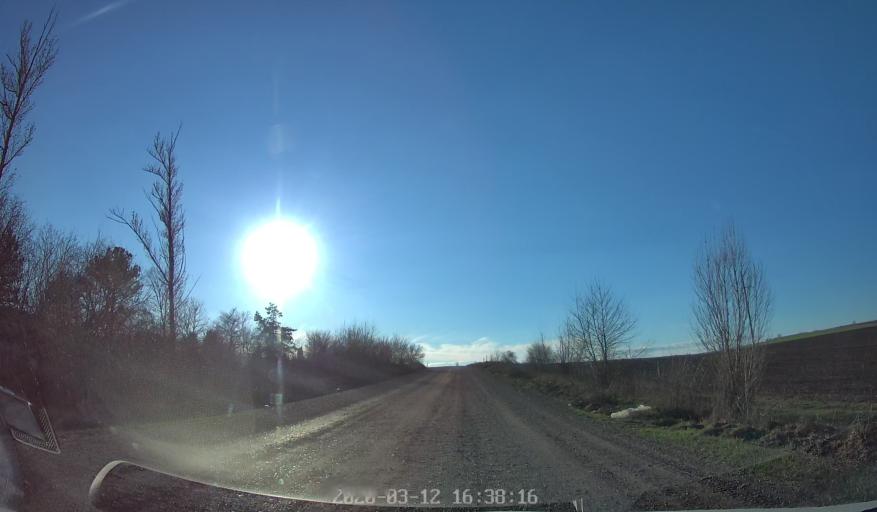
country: MD
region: Anenii Noi
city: Anenii Noi
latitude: 46.8163
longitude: 29.1804
